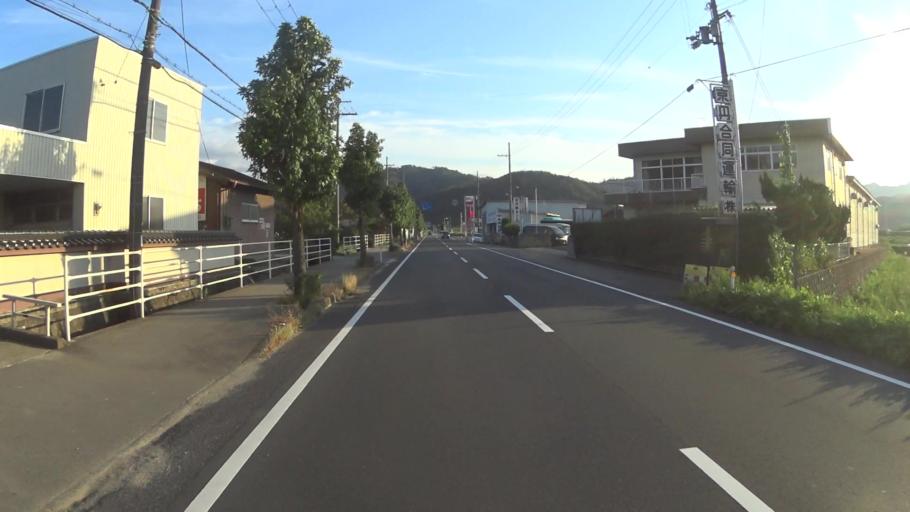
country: JP
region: Kyoto
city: Miyazu
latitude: 35.5720
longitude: 135.0975
